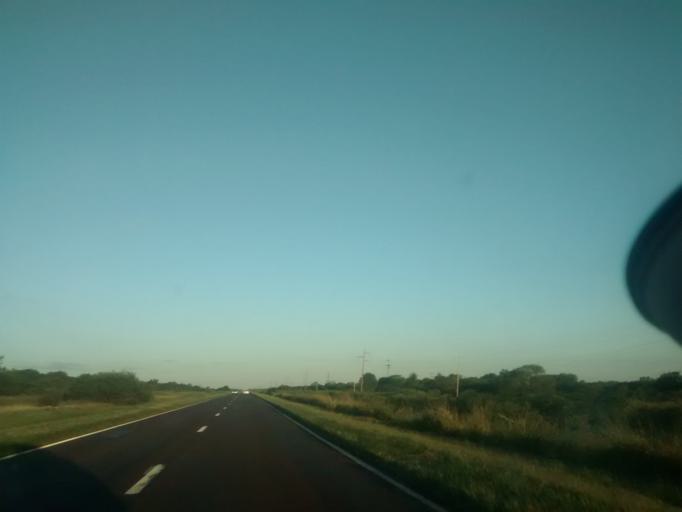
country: AR
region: Chaco
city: La Escondida
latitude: -27.0880
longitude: -59.6409
